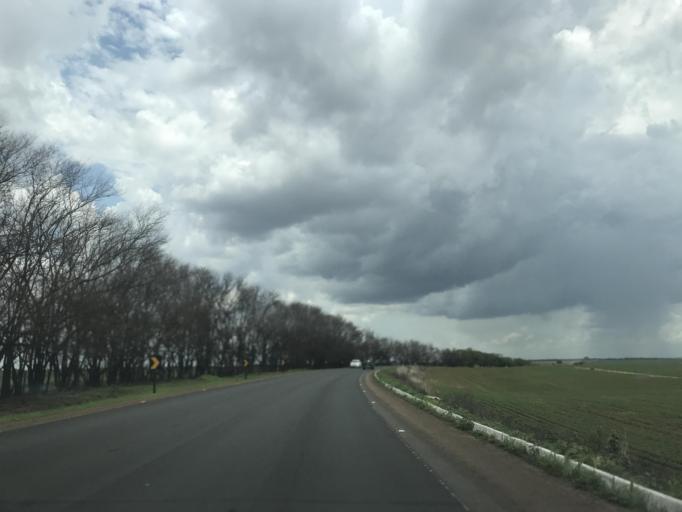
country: BR
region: Goias
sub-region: Vianopolis
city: Vianopolis
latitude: -16.8069
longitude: -48.5188
